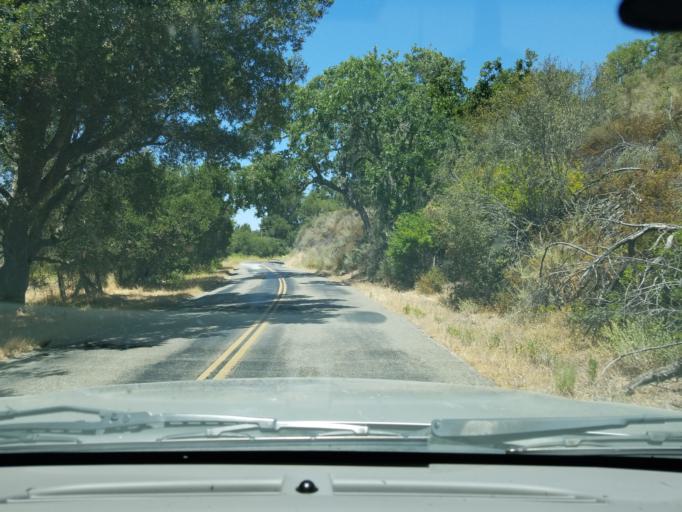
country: US
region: California
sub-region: Monterey County
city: Carmel Valley Village
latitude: 36.4228
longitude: -121.6160
